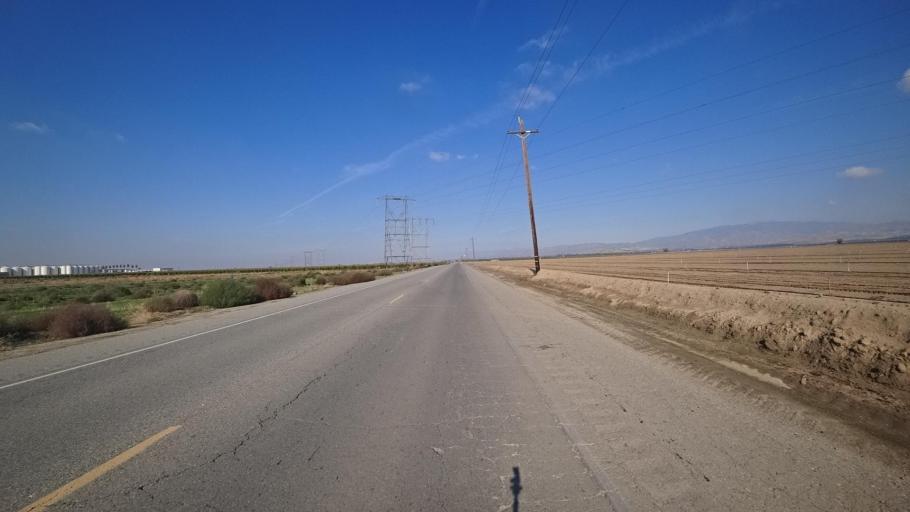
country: US
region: California
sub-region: Kern County
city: Arvin
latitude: 35.2544
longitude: -118.8248
